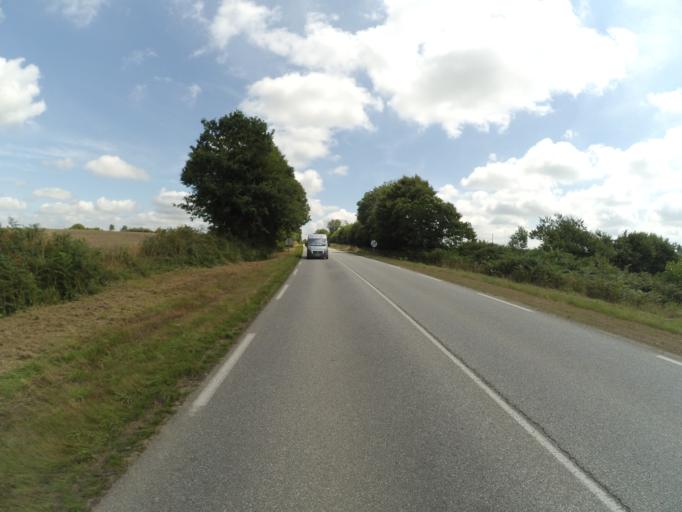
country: FR
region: Brittany
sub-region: Departement du Finistere
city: Saint-Yvi
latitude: 47.9702
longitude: -3.9724
